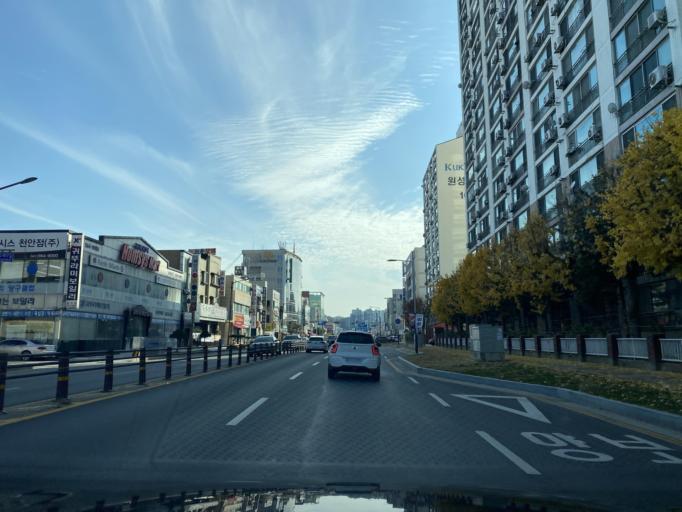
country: KR
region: Chungcheongnam-do
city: Cheonan
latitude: 36.8026
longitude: 127.1589
